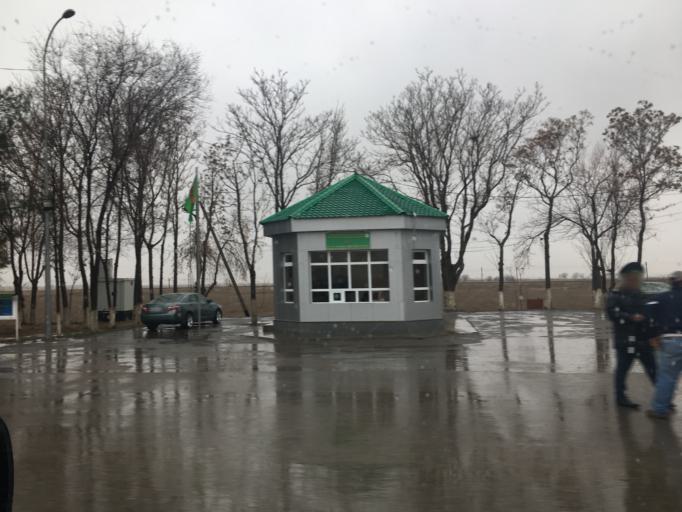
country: TM
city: Murgab
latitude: 37.5318
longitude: 61.8936
